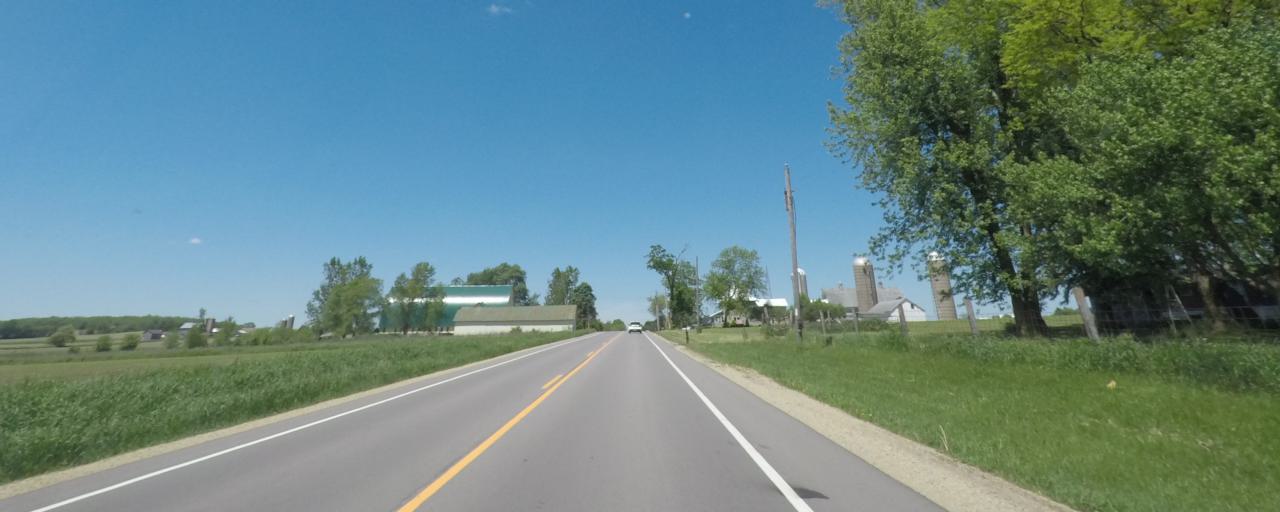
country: US
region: Wisconsin
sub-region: Green County
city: Brooklyn
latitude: 42.8146
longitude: -89.3692
